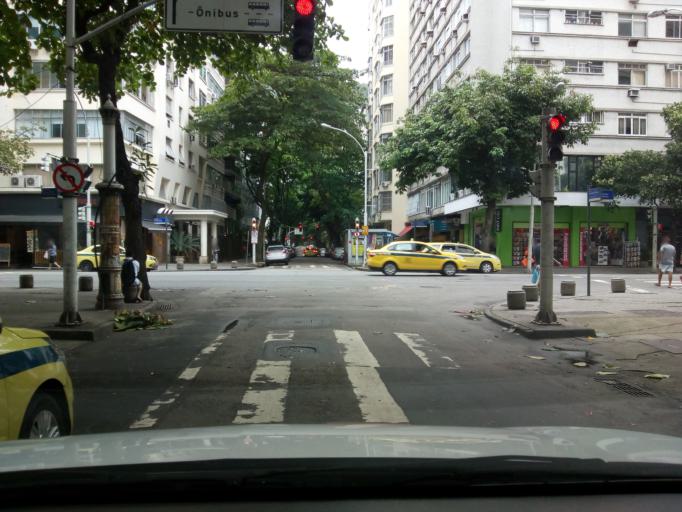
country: BR
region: Rio de Janeiro
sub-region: Rio De Janeiro
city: Rio de Janeiro
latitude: -22.9676
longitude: -43.1817
